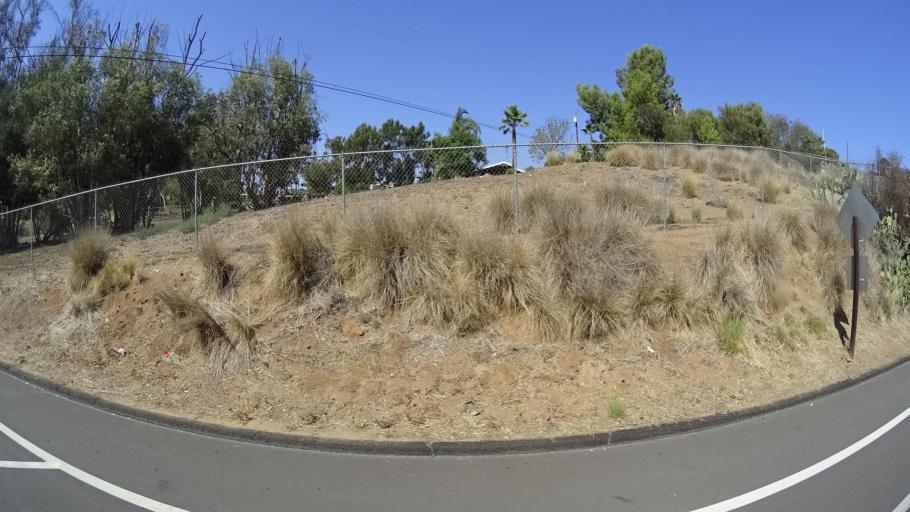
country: US
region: California
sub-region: San Diego County
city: Granite Hills
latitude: 32.7862
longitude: -116.9109
